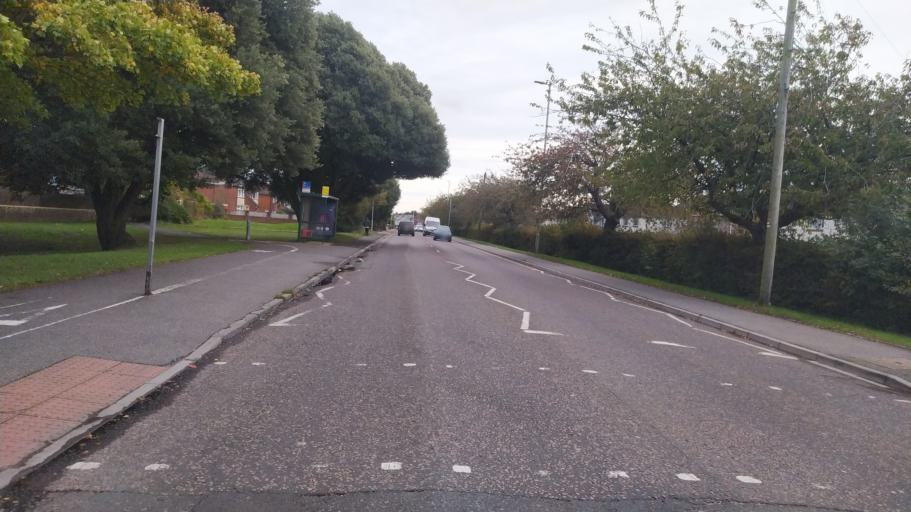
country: GB
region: England
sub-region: Dorset
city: Parkstone
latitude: 50.7493
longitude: -1.9215
